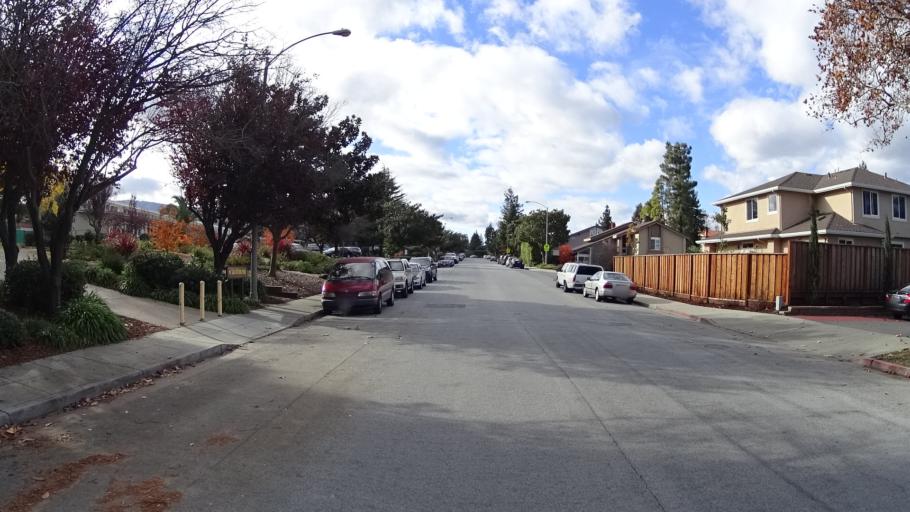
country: US
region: California
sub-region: Santa Clara County
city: Sunnyvale
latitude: 37.3503
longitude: -122.0562
